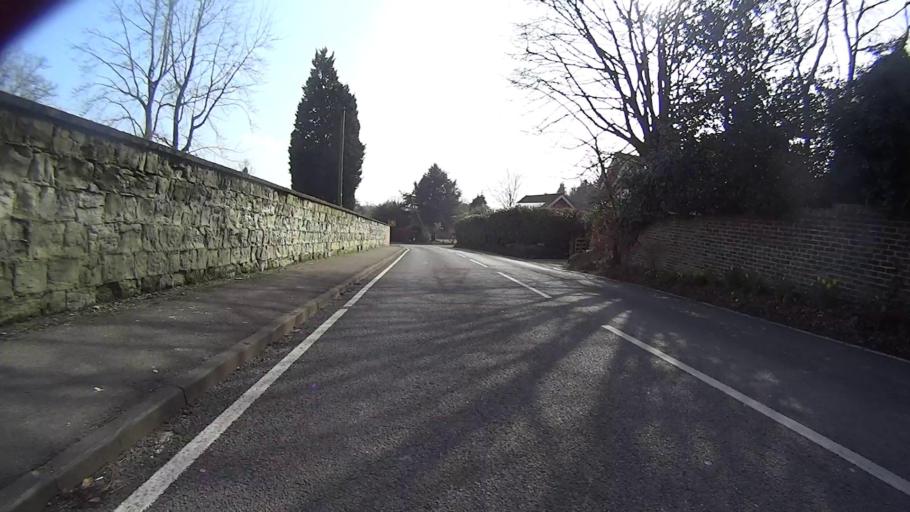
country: GB
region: England
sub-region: Surrey
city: Headley
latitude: 51.2413
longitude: -0.2687
